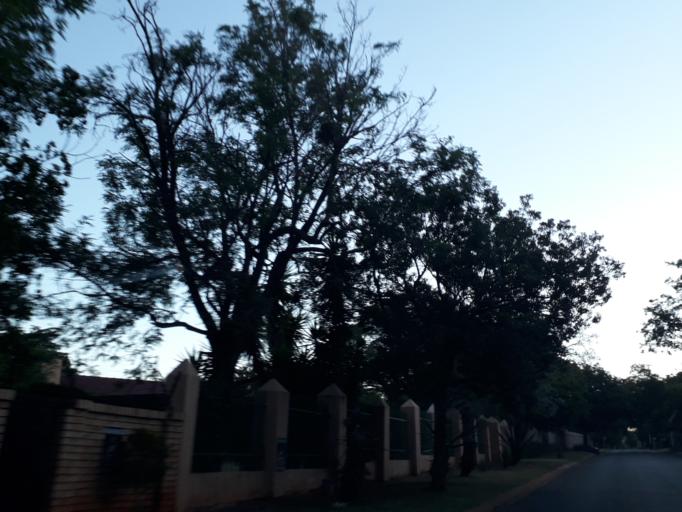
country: ZA
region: Gauteng
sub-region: City of Johannesburg Metropolitan Municipality
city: Roodepoort
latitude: -26.1267
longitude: 27.9452
